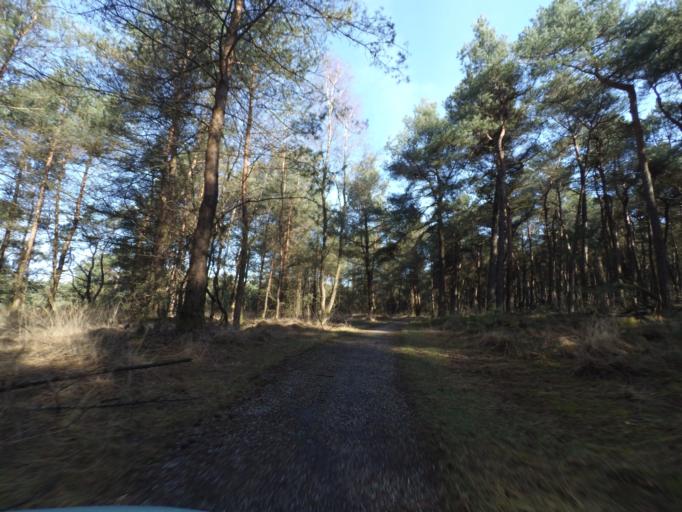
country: NL
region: Gelderland
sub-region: Gemeente Ede
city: Harskamp
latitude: 52.1555
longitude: 5.7342
